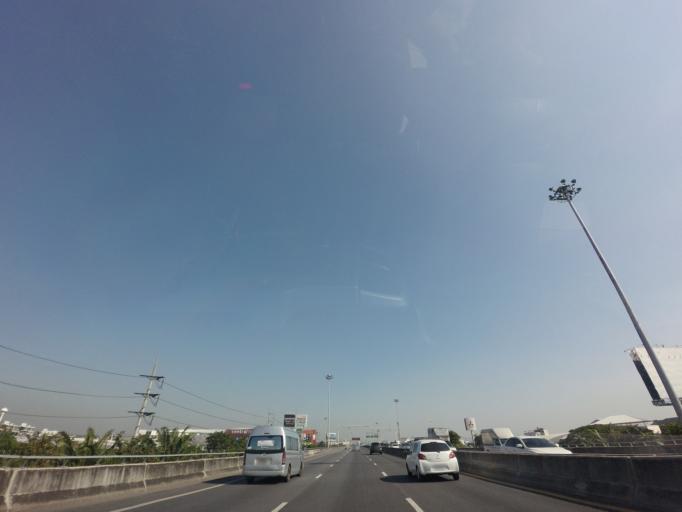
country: TH
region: Bangkok
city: Lat Phrao
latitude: 13.7991
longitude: 100.6145
